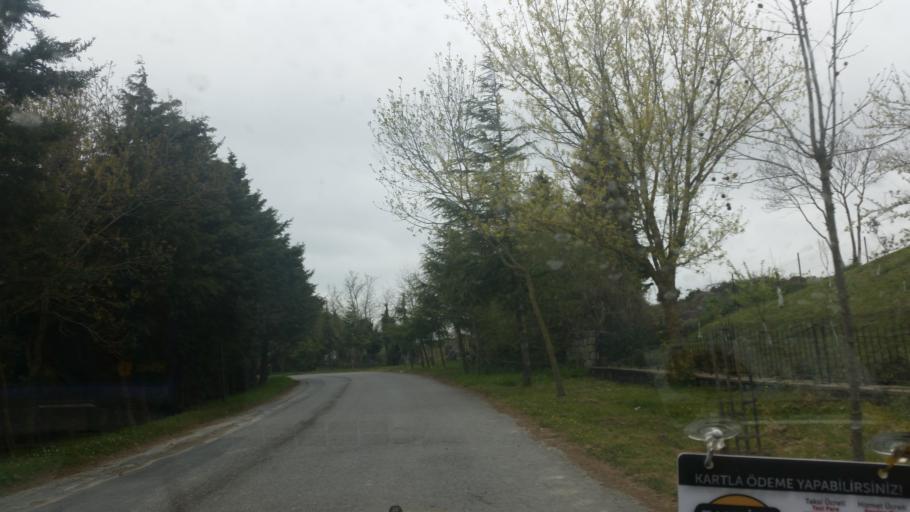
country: TR
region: Istanbul
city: Boyalik
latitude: 41.2869
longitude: 28.6070
